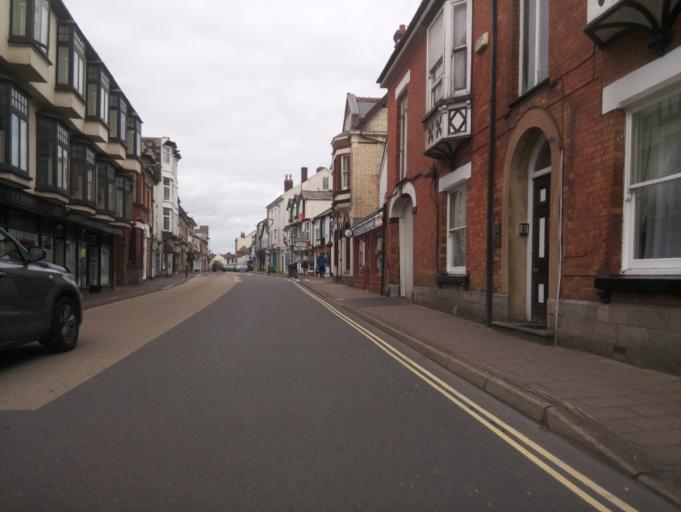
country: GB
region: England
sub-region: Devon
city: Cullompton
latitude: 50.8554
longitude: -3.3927
